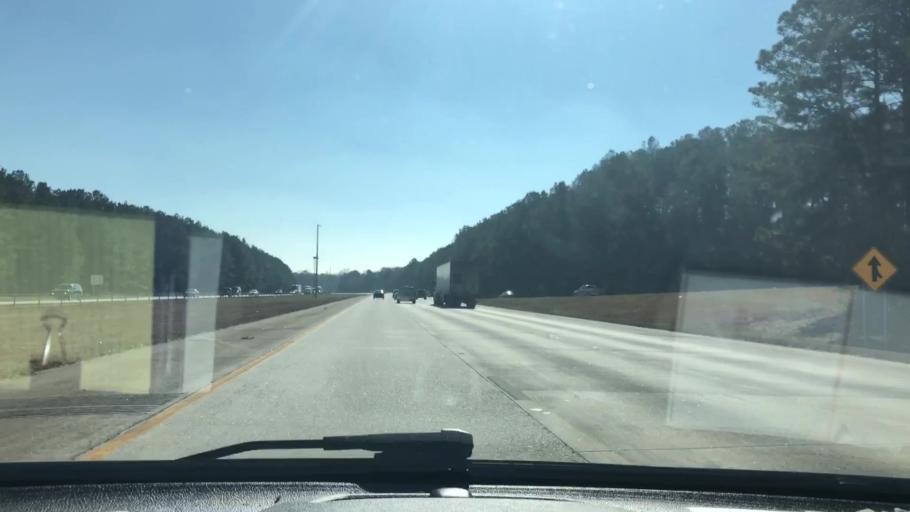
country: US
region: Georgia
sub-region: Clayton County
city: Lake City
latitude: 33.6096
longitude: -84.2964
